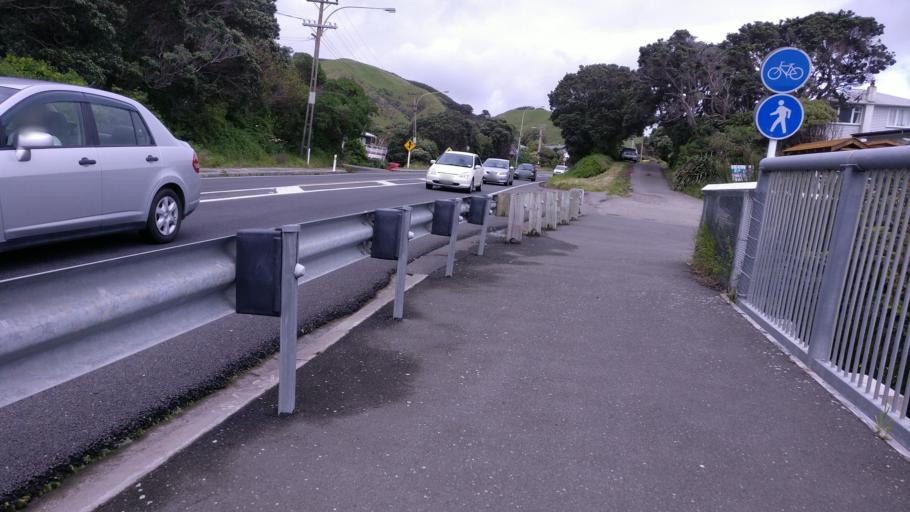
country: NZ
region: Wellington
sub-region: Porirua City
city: Porirua
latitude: -41.0310
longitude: 174.8967
